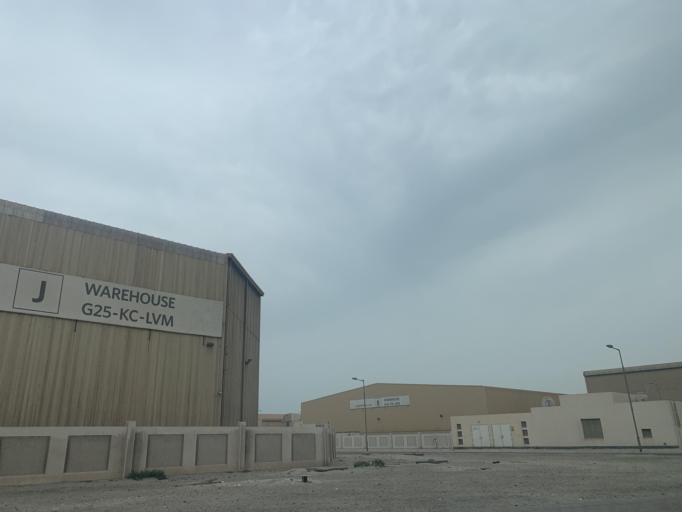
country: BH
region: Muharraq
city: Al Hadd
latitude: 26.2035
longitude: 50.6842
